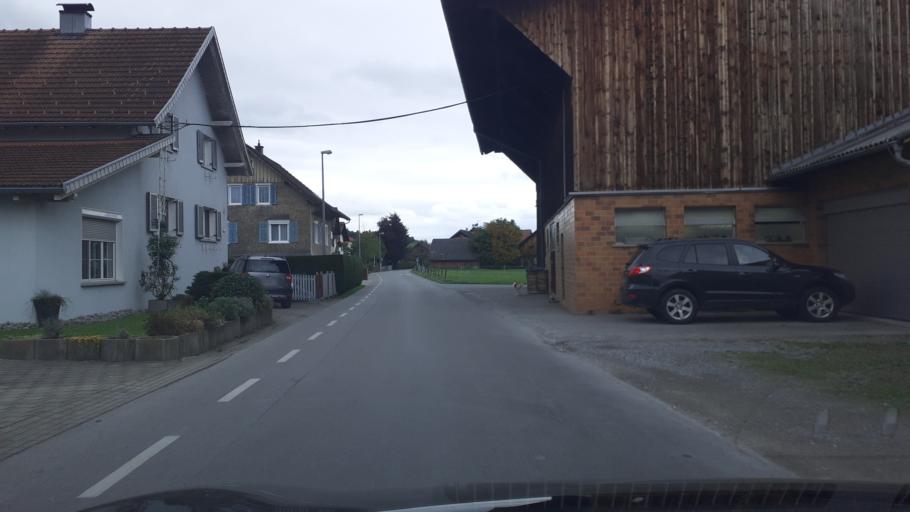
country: AT
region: Vorarlberg
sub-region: Politischer Bezirk Bregenz
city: Gaissau
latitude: 47.4667
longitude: 9.5964
